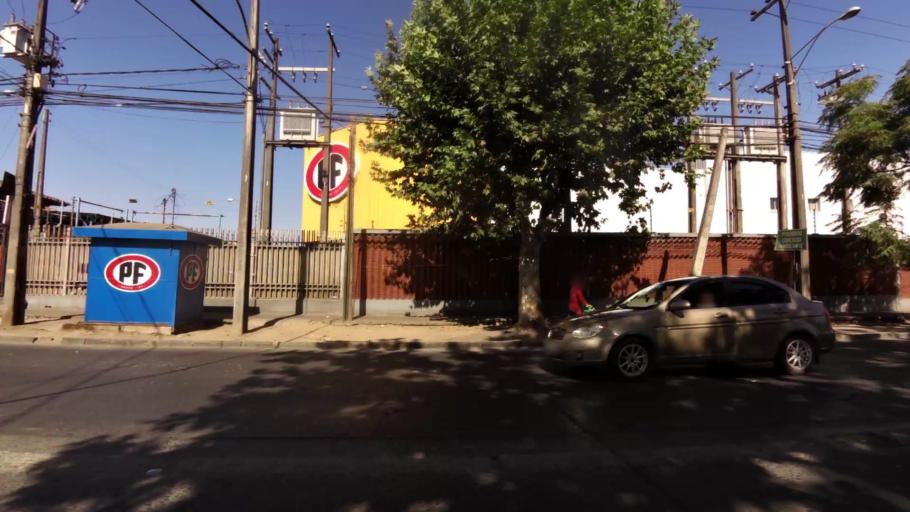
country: CL
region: Maule
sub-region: Provincia de Talca
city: Talca
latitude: -35.4245
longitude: -71.6499
